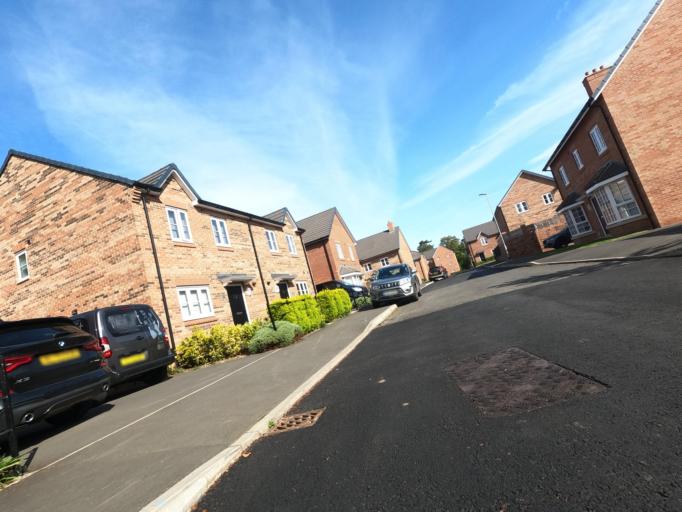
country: GB
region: England
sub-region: Northumberland
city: Morpeth
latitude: 55.1740
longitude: -1.6852
